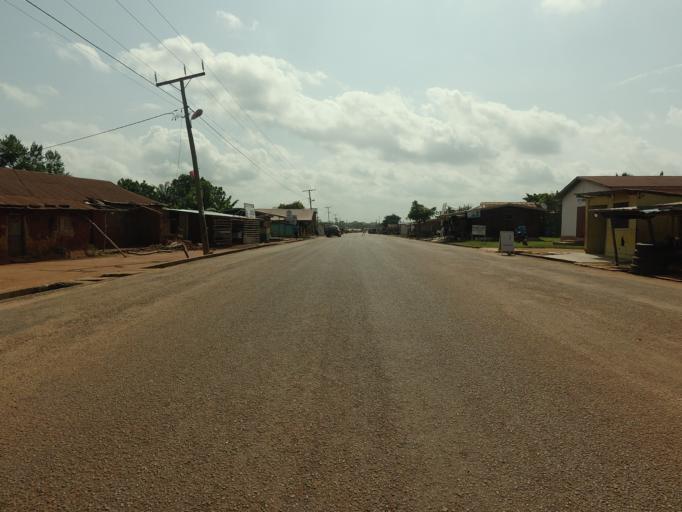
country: TG
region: Maritime
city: Tsevie
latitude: 6.3618
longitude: 0.8592
